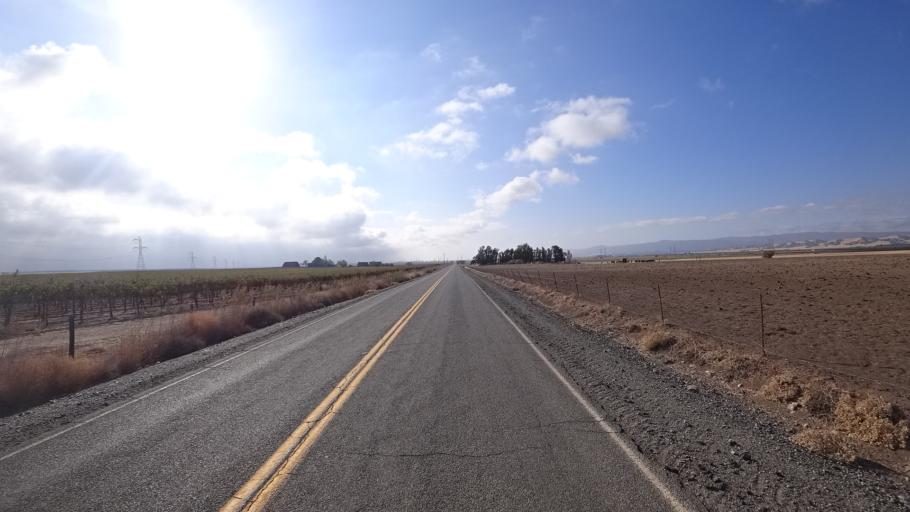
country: US
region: California
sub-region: Yolo County
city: Esparto
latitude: 38.7866
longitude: -122.0071
